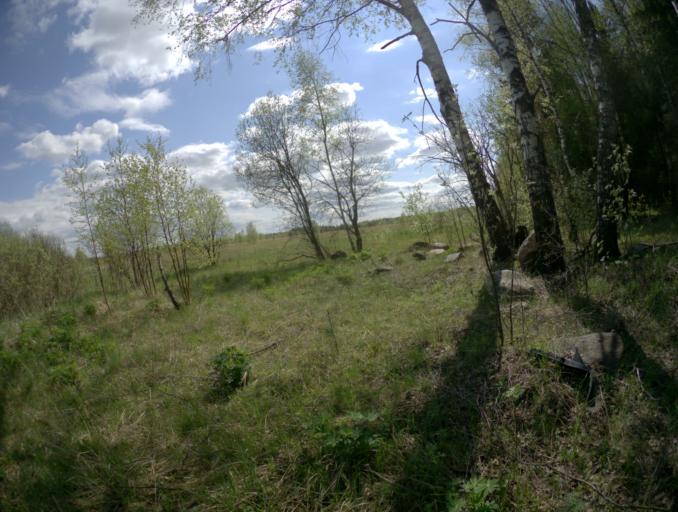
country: RU
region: Vladimir
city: Golovino
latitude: 55.9597
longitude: 40.4001
